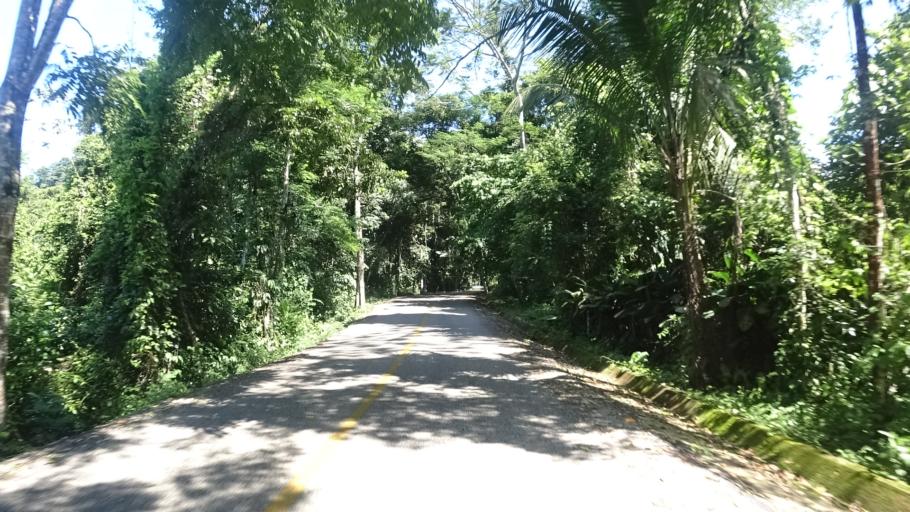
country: MX
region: Chiapas
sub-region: Salto de Agua
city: Belisario Dominguez
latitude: 17.3934
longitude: -92.0001
